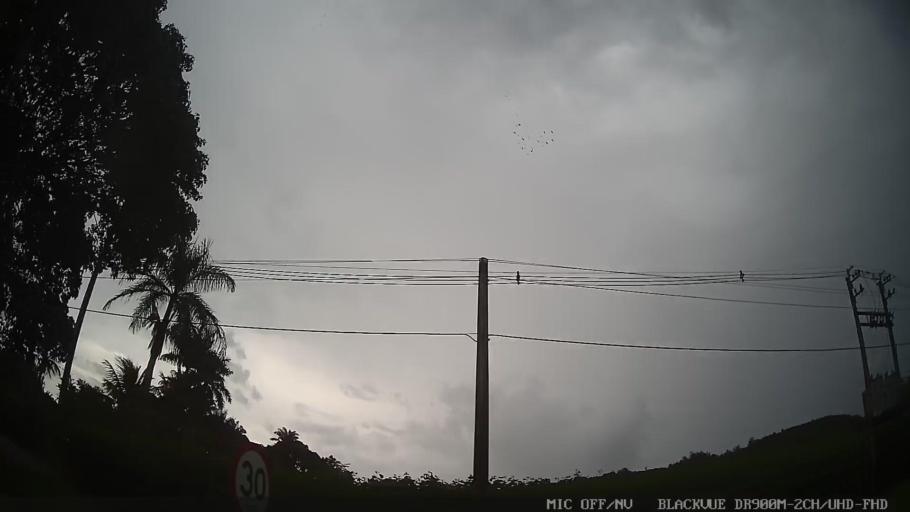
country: BR
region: Sao Paulo
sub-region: Pedreira
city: Pedreira
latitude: -22.7172
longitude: -46.8581
